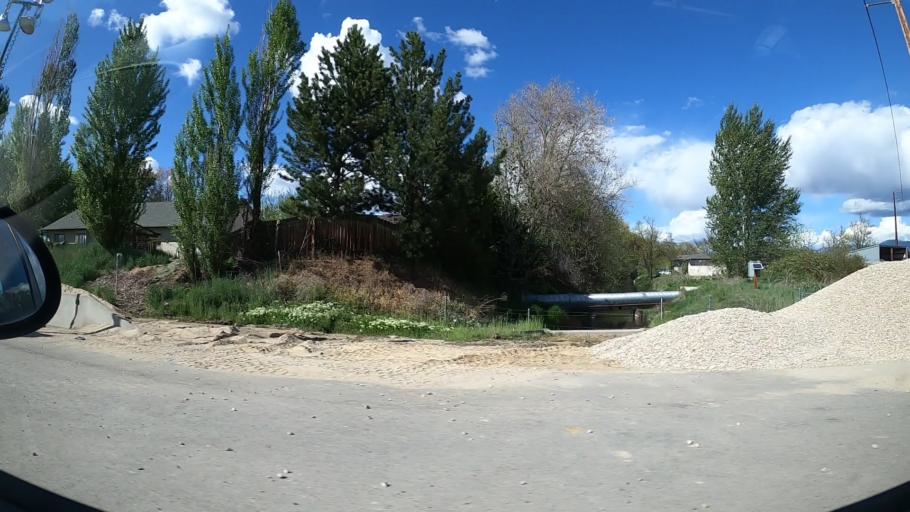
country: US
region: Idaho
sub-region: Ada County
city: Eagle
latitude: 43.6912
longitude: -116.3559
